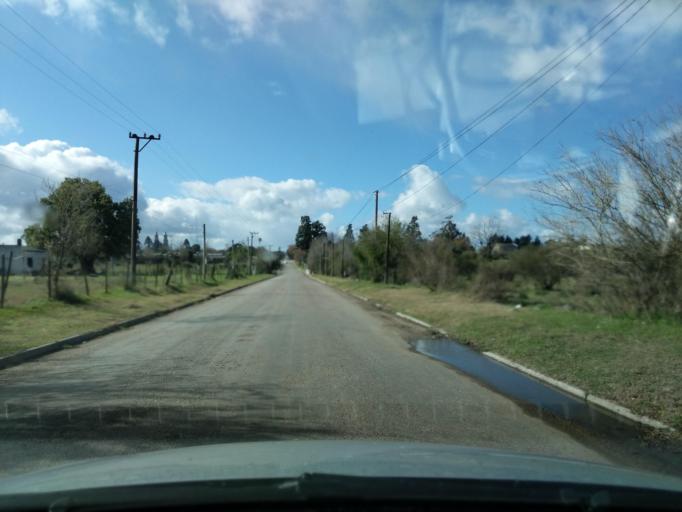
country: UY
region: Florida
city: Florida
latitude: -34.1089
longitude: -56.2200
